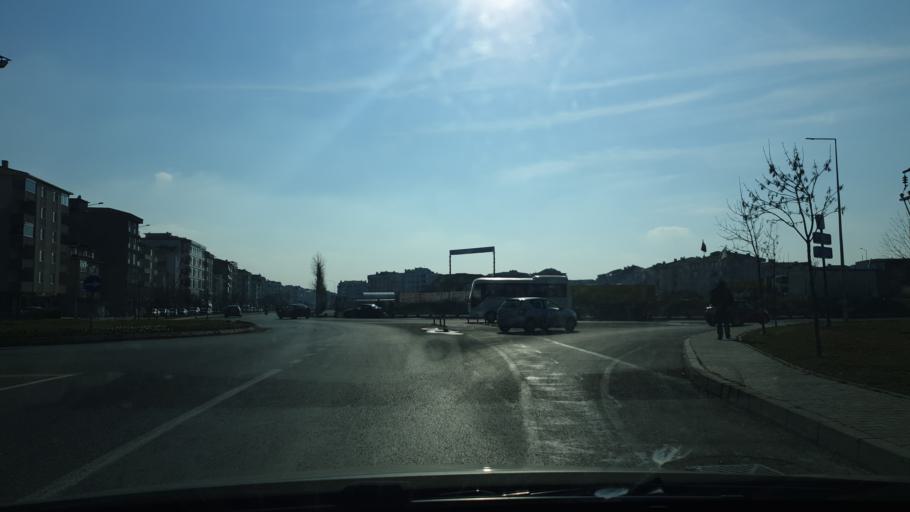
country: TR
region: Tekirdag
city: Cerkezkoey
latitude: 41.2917
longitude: 27.9934
